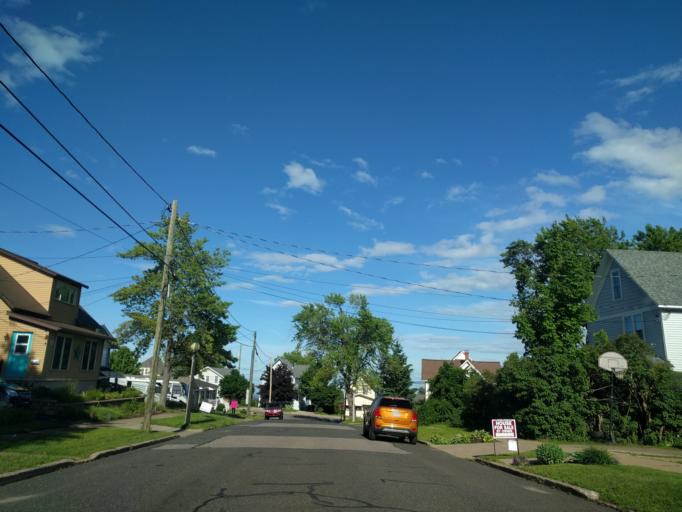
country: US
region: Michigan
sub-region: Marquette County
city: Marquette
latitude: 46.5358
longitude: -87.3981
